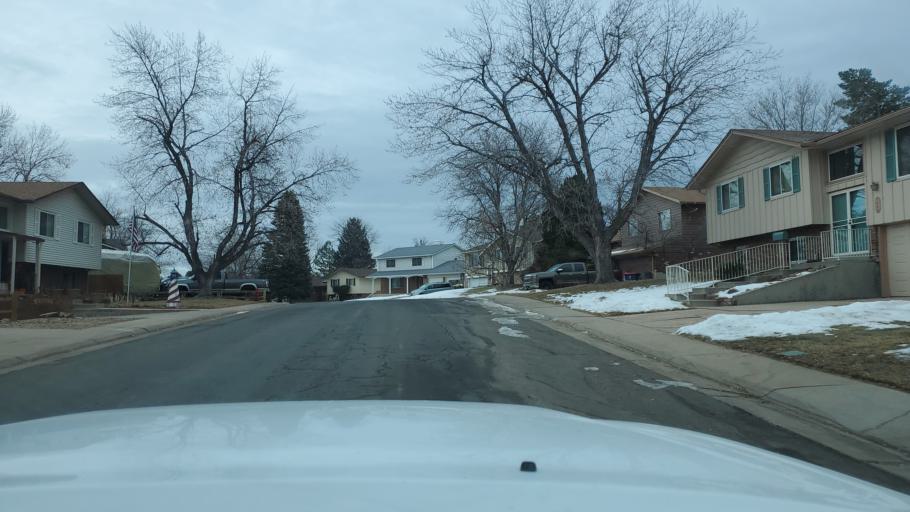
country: US
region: Colorado
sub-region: Arapahoe County
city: Castlewood
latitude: 39.5916
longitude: -104.9021
